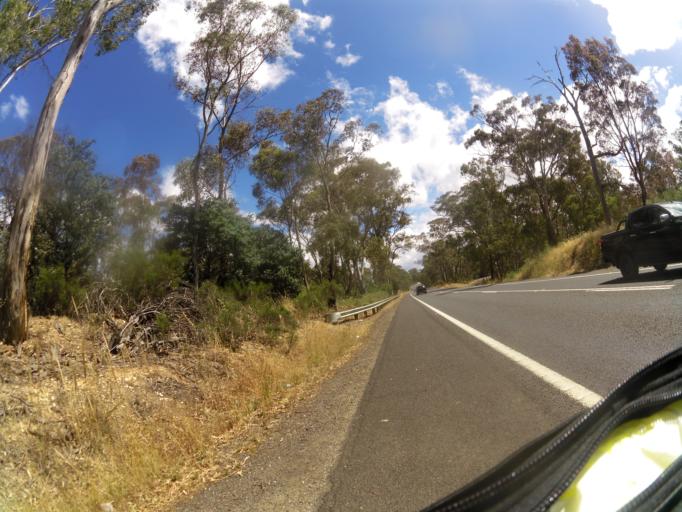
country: AU
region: Victoria
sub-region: Mount Alexander
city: Castlemaine
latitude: -37.0339
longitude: 144.2312
